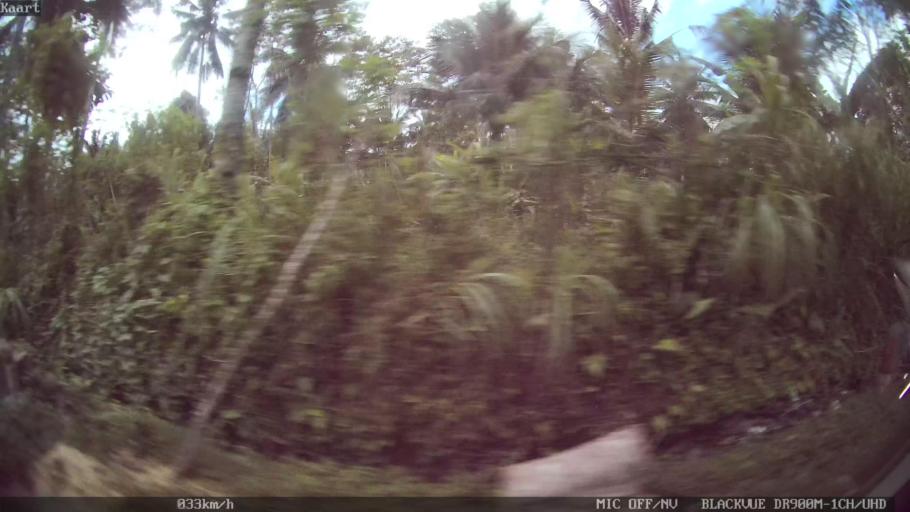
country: ID
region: Bali
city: Banjar Petak
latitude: -8.4549
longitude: 115.3194
